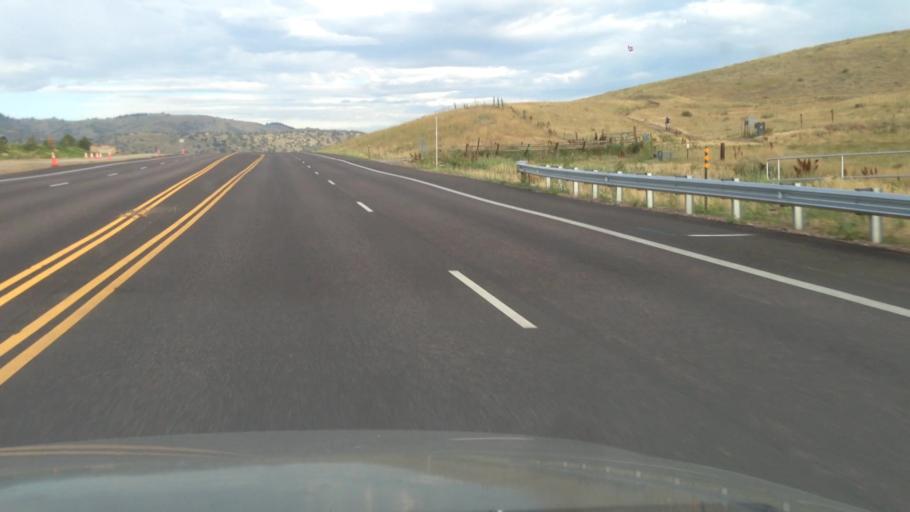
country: US
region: Colorado
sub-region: Jefferson County
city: West Pleasant View
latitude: 39.6804
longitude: -105.1671
